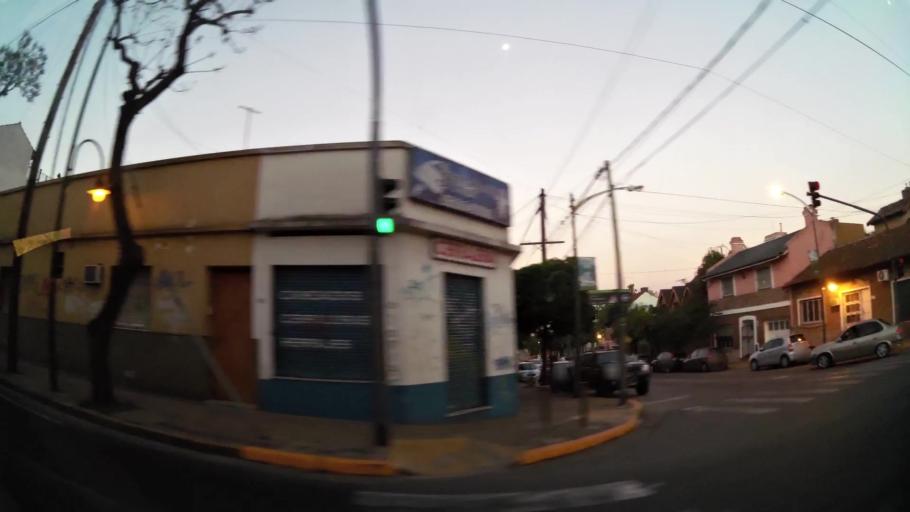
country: AR
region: Buenos Aires
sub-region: Partido de Tigre
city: Tigre
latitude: -34.4385
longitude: -58.5567
